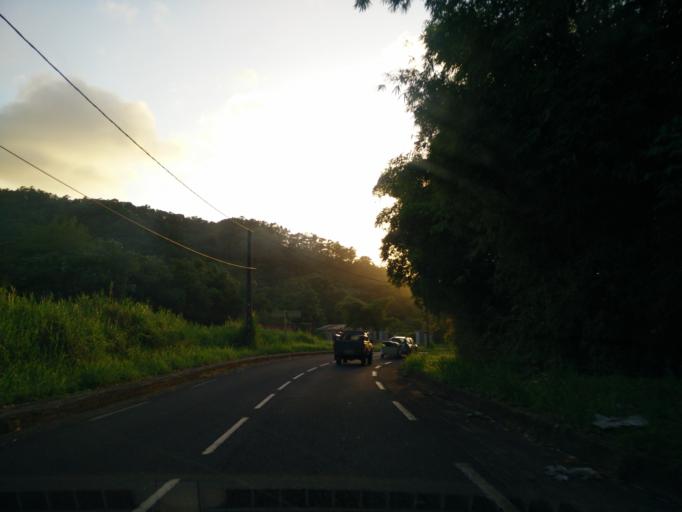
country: MQ
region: Martinique
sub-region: Martinique
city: Le Morne-Rouge
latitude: 14.7498
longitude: -61.1032
